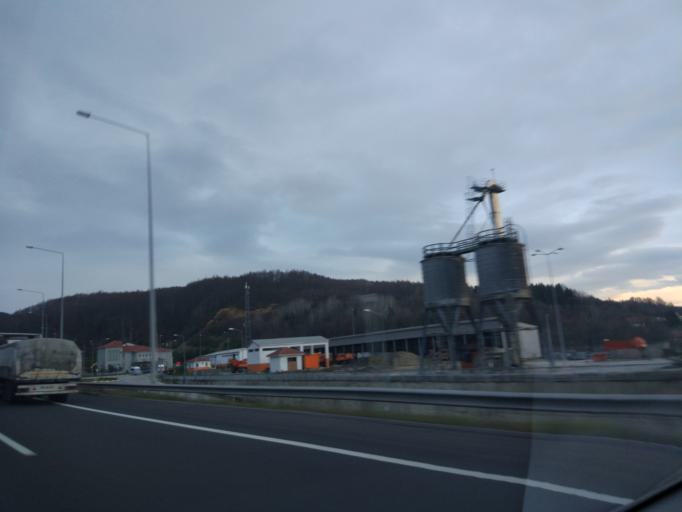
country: TR
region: Duzce
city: Kaynasli
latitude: 40.7339
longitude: 31.4459
